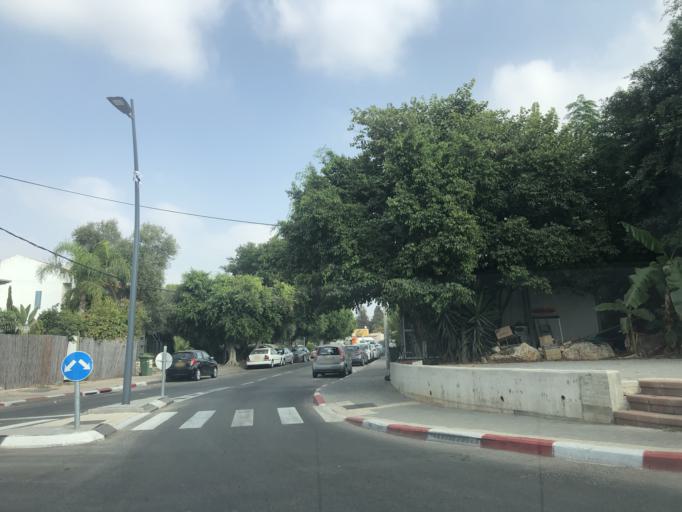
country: IL
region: Central District
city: Rosh Ha'Ayin
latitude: 32.0963
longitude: 34.9486
